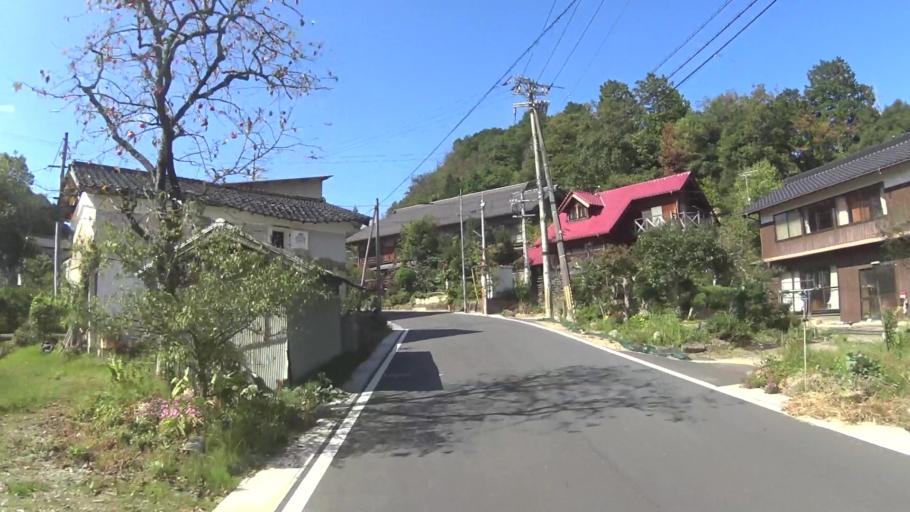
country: JP
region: Hyogo
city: Toyooka
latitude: 35.5932
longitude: 134.9544
